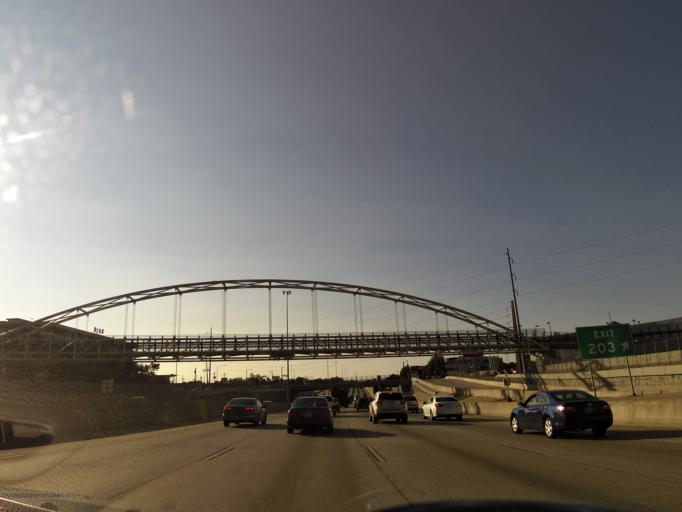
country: US
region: Colorado
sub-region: Arapahoe County
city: Glendale
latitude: 39.6806
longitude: -104.9362
